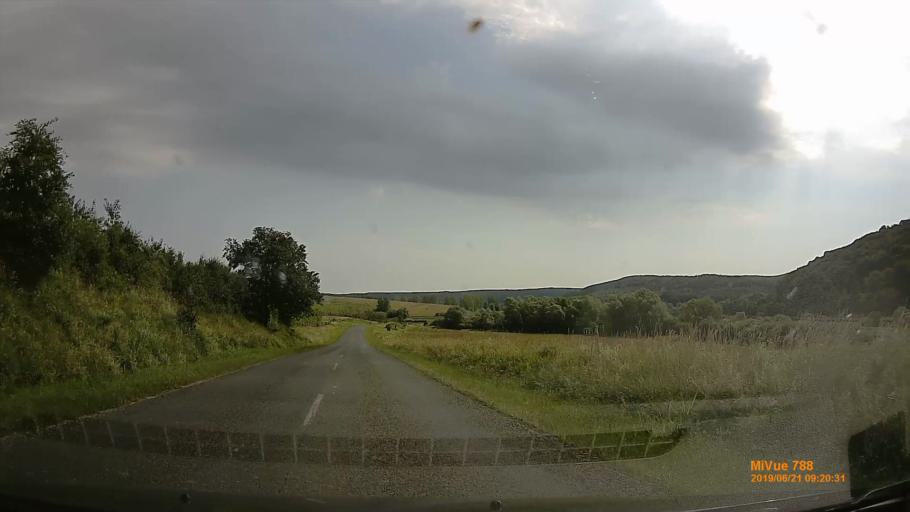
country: HU
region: Somogy
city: Taszar
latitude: 46.2353
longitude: 17.8721
